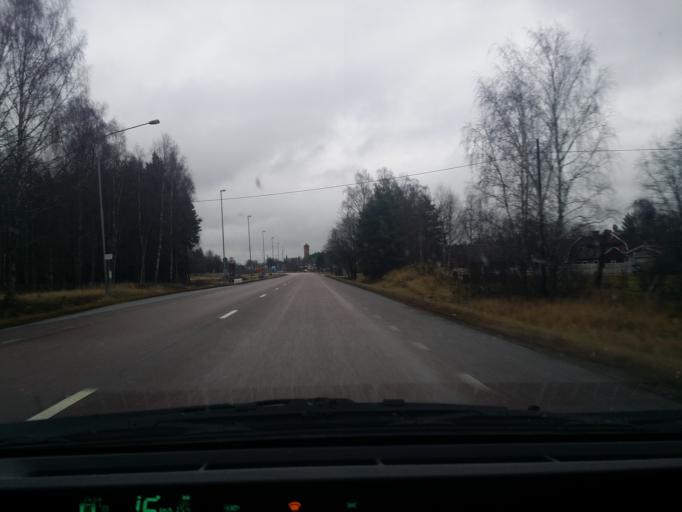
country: SE
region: Vaestmanland
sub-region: Sala Kommun
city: Sala
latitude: 59.9052
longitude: 16.5813
